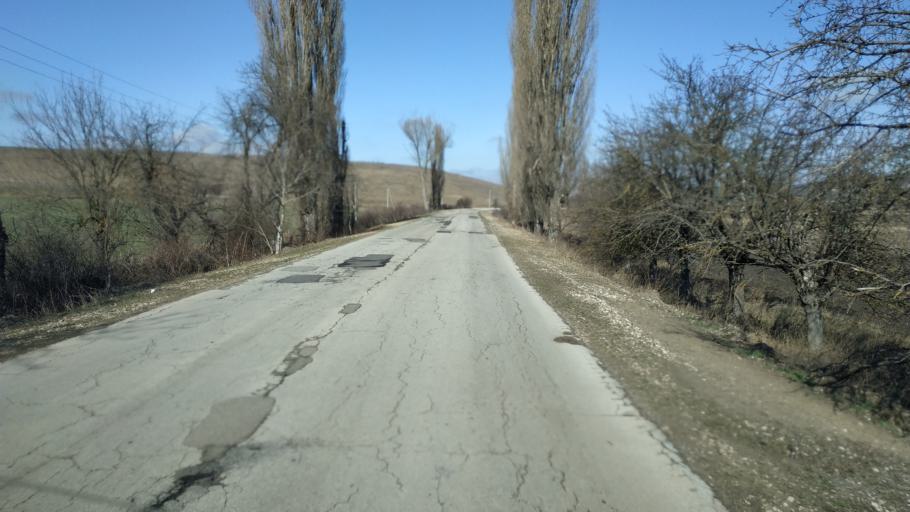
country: MD
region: Straseni
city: Straseni
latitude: 46.9915
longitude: 28.5537
